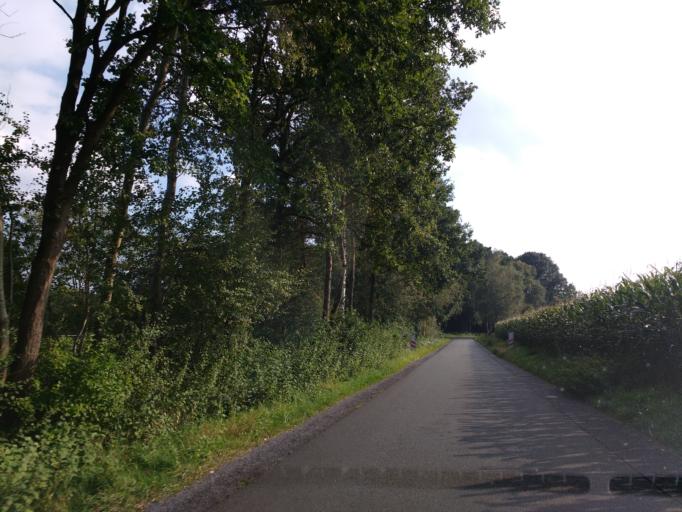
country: DE
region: North Rhine-Westphalia
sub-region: Regierungsbezirk Detmold
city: Hovelhof
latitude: 51.7866
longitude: 8.7011
